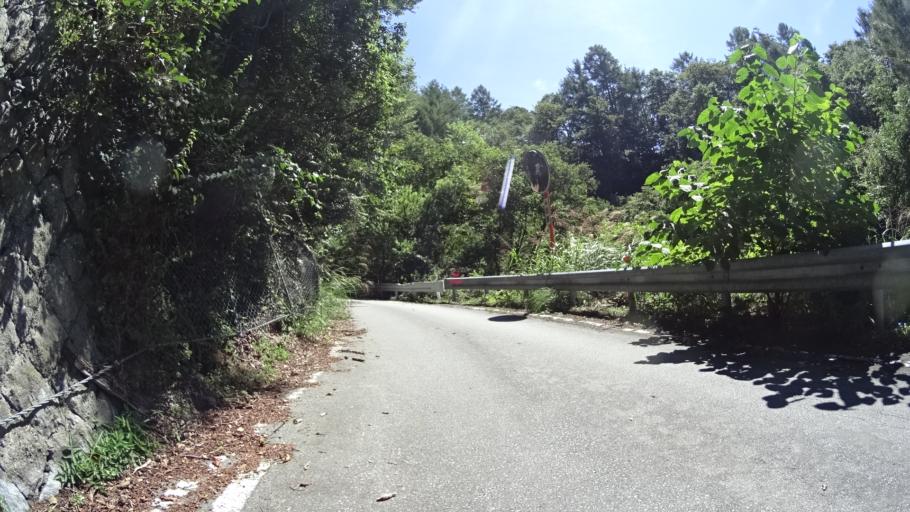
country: JP
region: Yamanashi
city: Enzan
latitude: 35.7436
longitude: 138.8218
